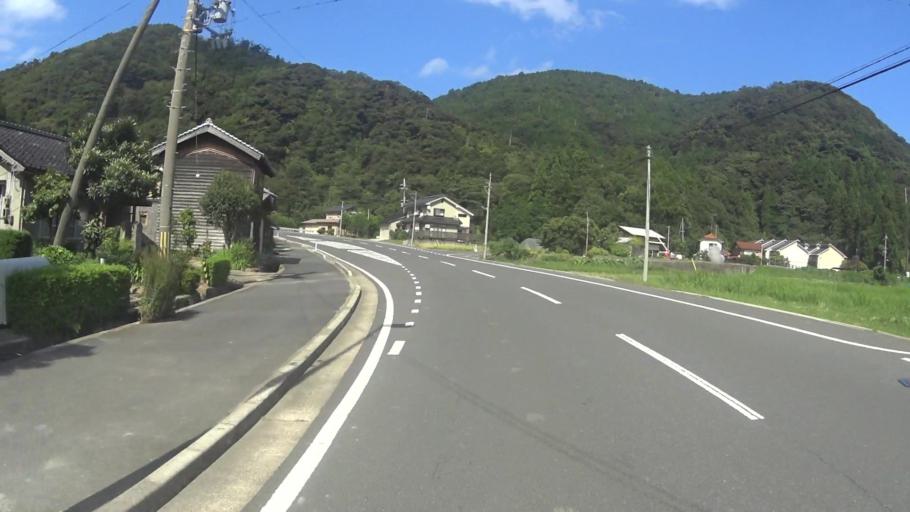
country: JP
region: Kyoto
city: Miyazu
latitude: 35.7311
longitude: 135.2576
